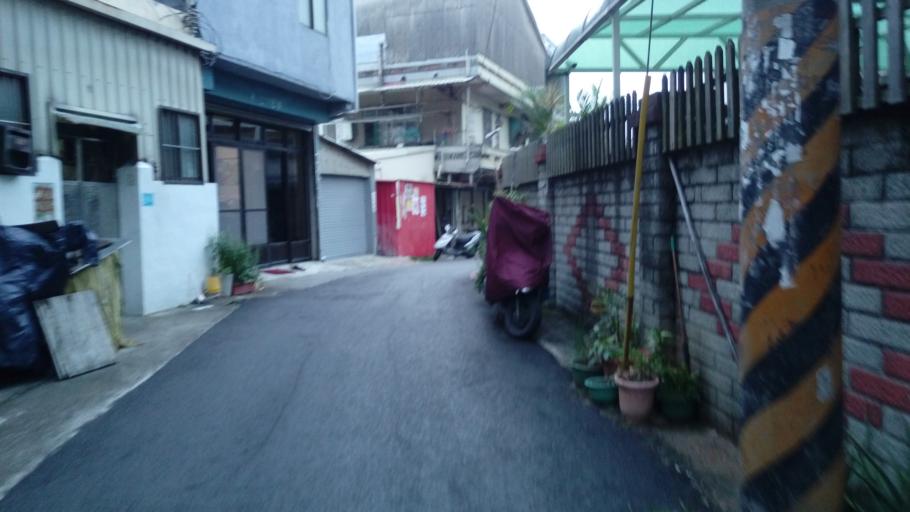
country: TW
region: Taiwan
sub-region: Hsinchu
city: Hsinchu
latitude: 24.8045
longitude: 120.9479
